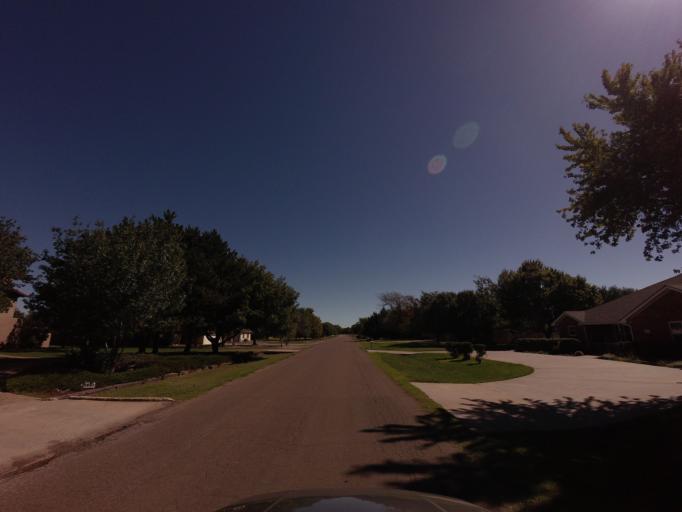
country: US
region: New Mexico
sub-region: Curry County
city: Clovis
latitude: 34.4276
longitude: -103.1746
